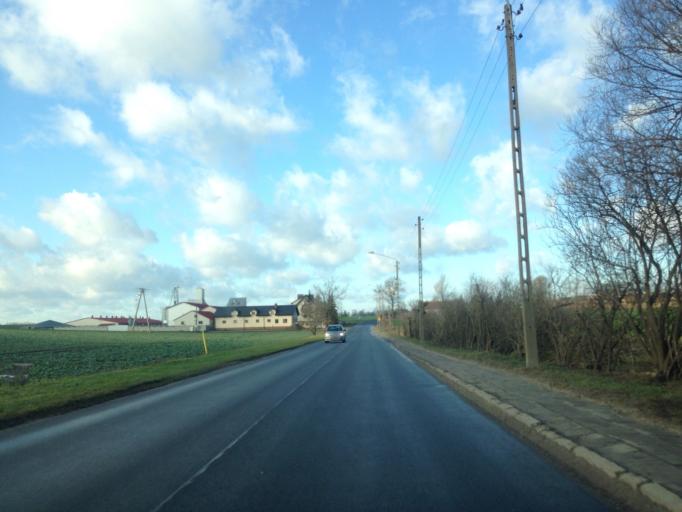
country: PL
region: Kujawsko-Pomorskie
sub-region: Powiat grudziadzki
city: Lasin
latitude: 53.5270
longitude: 19.0776
